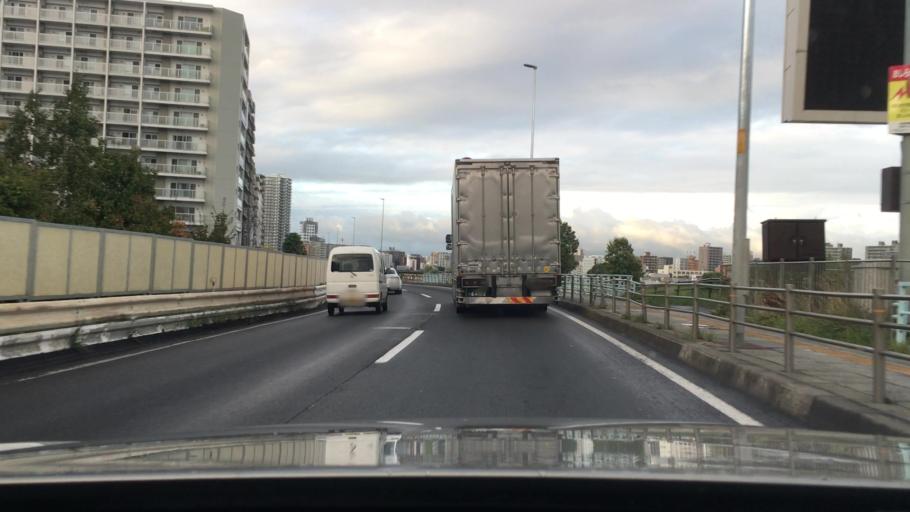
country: JP
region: Hokkaido
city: Sapporo
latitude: 43.0412
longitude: 141.3576
